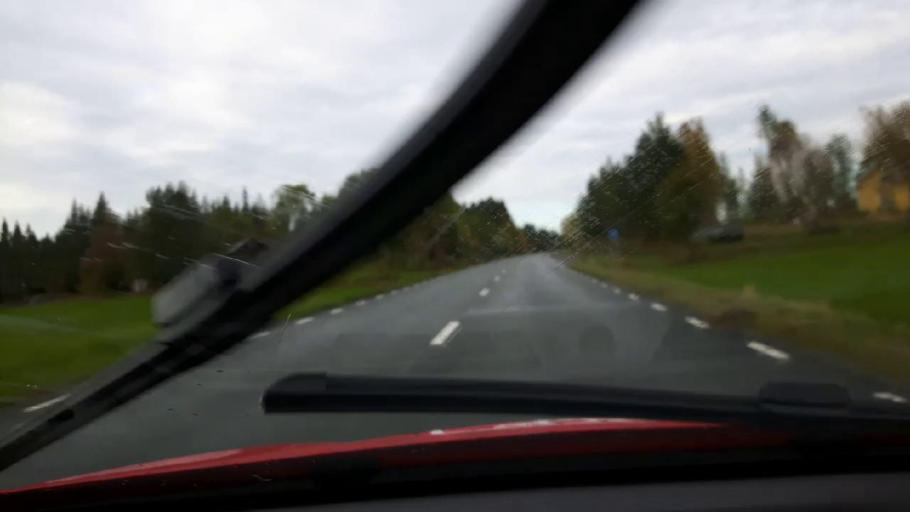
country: SE
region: Jaemtland
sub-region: Krokoms Kommun
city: Krokom
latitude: 63.1046
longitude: 14.2968
